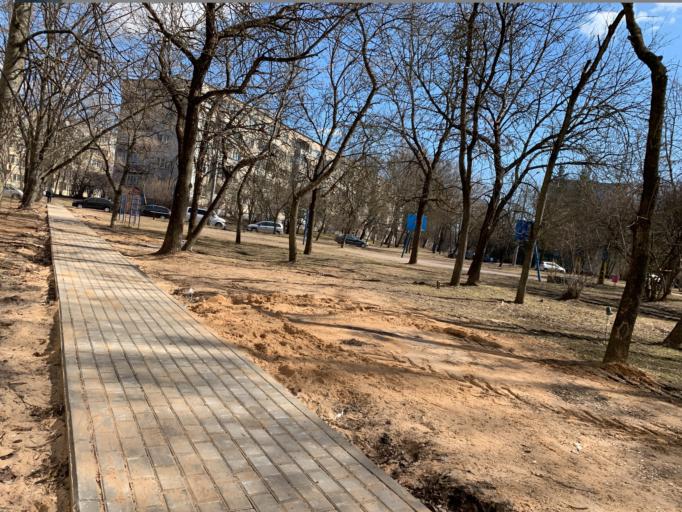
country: BY
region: Minsk
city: Minsk
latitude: 53.9300
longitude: 27.5914
